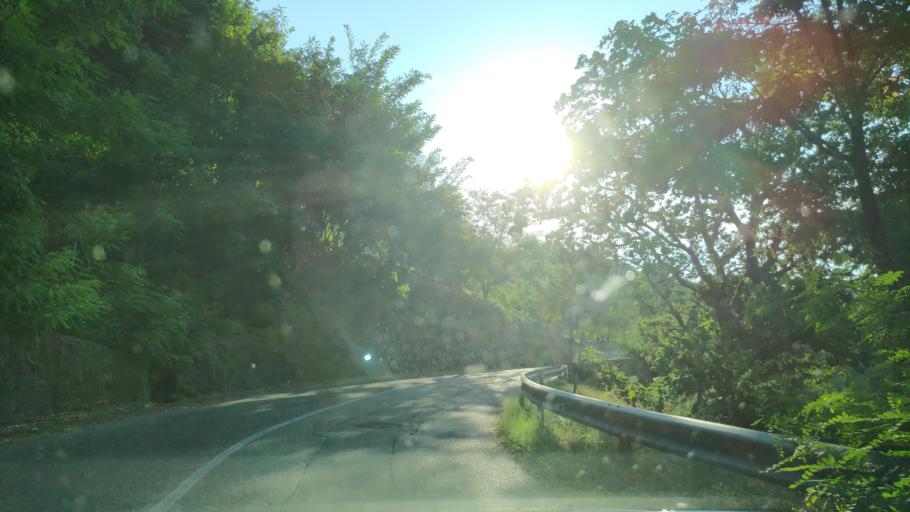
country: IT
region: Calabria
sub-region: Provincia di Catanzaro
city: Satriano
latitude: 38.6706
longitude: 16.4854
